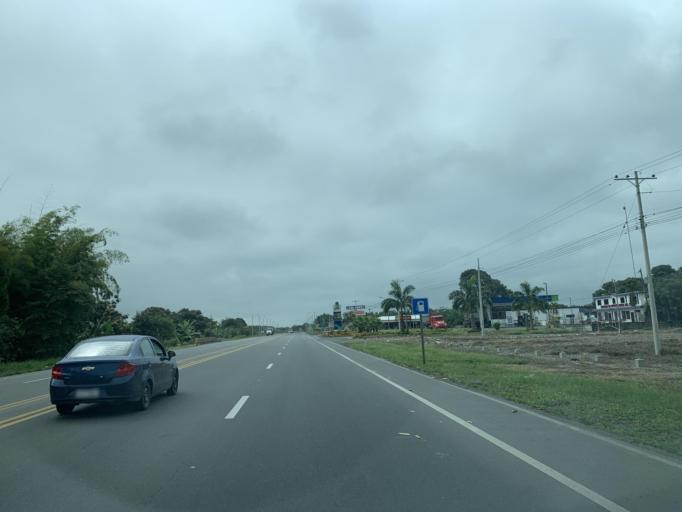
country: EC
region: Guayas
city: Coronel Marcelino Mariduena
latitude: -2.3144
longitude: -79.4720
